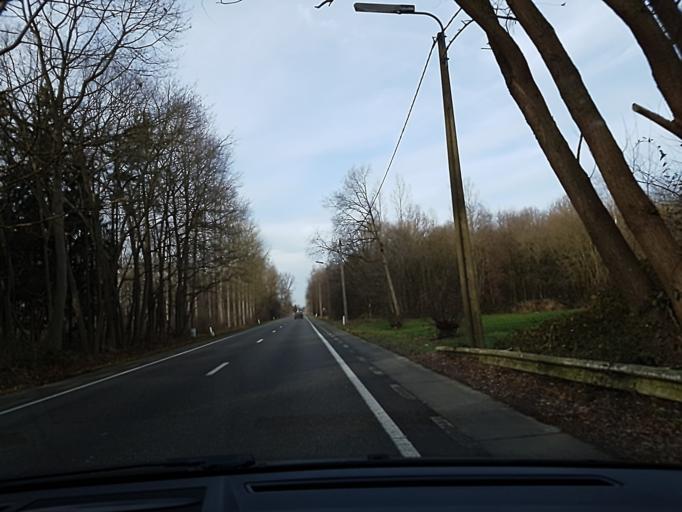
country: BE
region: Flanders
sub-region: Provincie Vlaams-Brabant
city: Rotselaar
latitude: 50.9606
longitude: 4.6999
